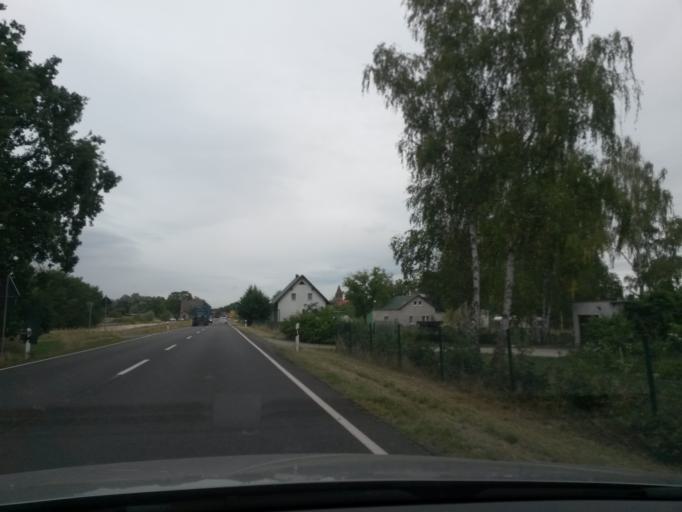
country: DE
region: Saxony-Anhalt
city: Klietz
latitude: 52.6627
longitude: 12.0610
